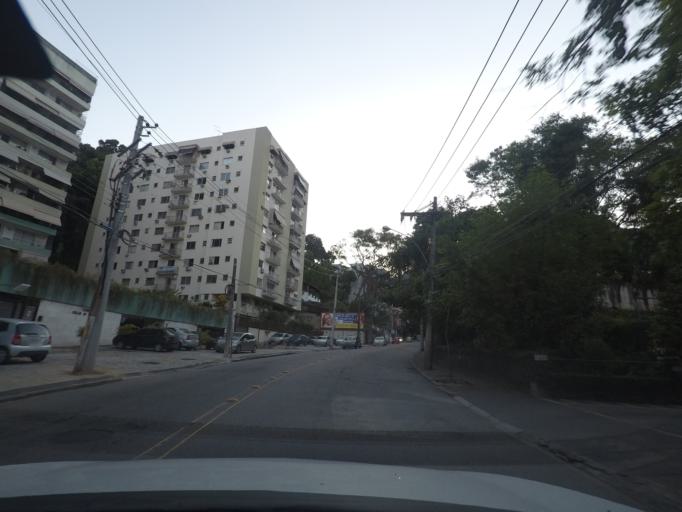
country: BR
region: Rio de Janeiro
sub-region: Rio De Janeiro
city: Rio de Janeiro
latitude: -22.9464
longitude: -43.2557
